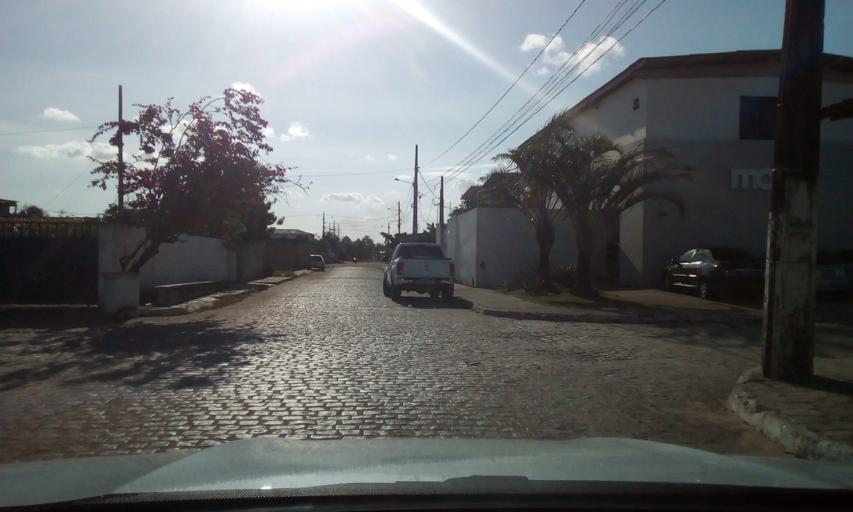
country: BR
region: Paraiba
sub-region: Joao Pessoa
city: Joao Pessoa
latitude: -7.0771
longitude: -34.8517
